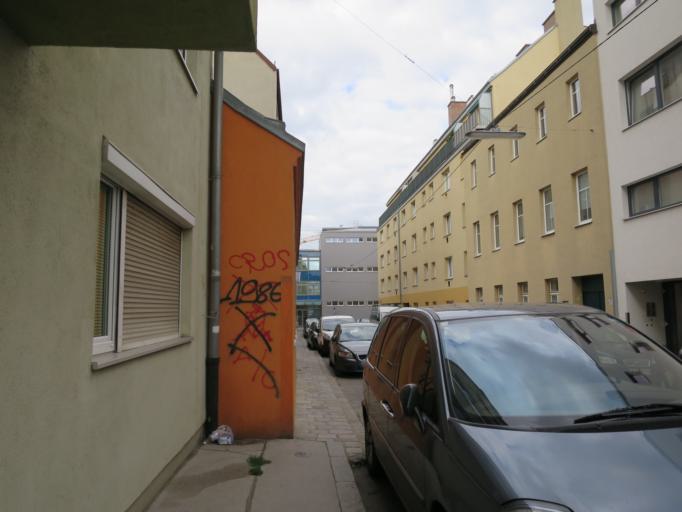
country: AT
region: Vienna
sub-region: Wien Stadt
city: Vienna
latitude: 48.2158
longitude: 16.3332
